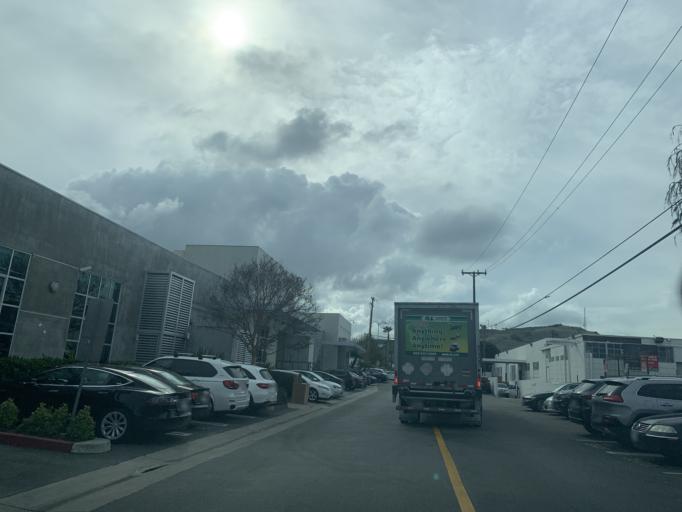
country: US
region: California
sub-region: Los Angeles County
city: Culver City
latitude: 34.0256
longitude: -118.3778
